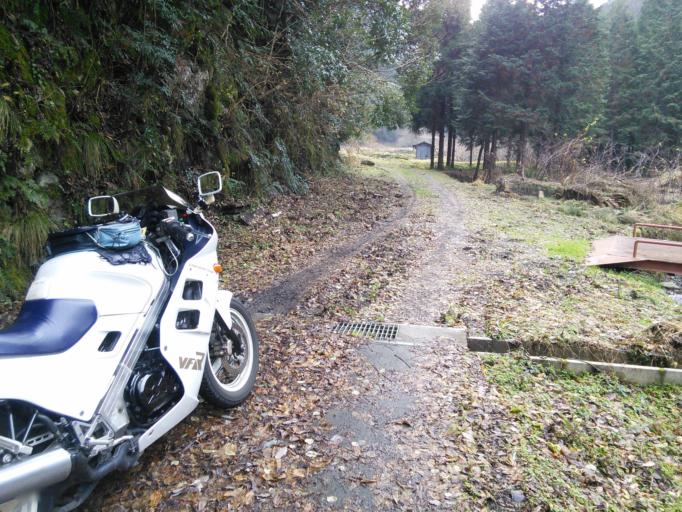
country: JP
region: Kyoto
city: Maizuru
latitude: 35.4139
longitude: 135.3022
